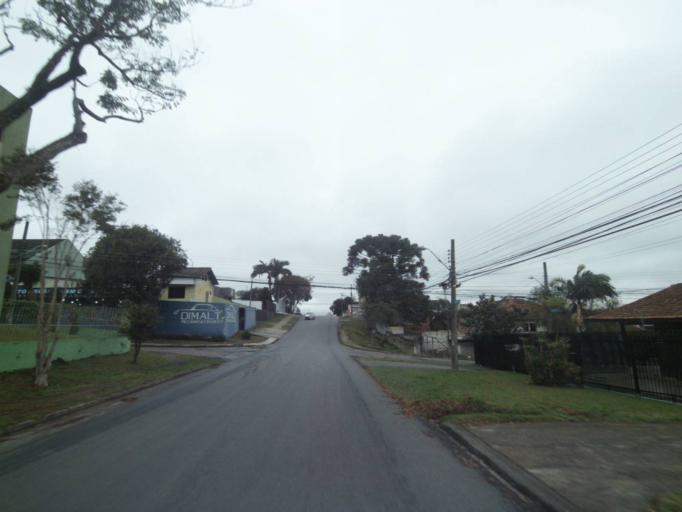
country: BR
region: Parana
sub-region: Curitiba
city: Curitiba
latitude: -25.5125
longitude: -49.2991
